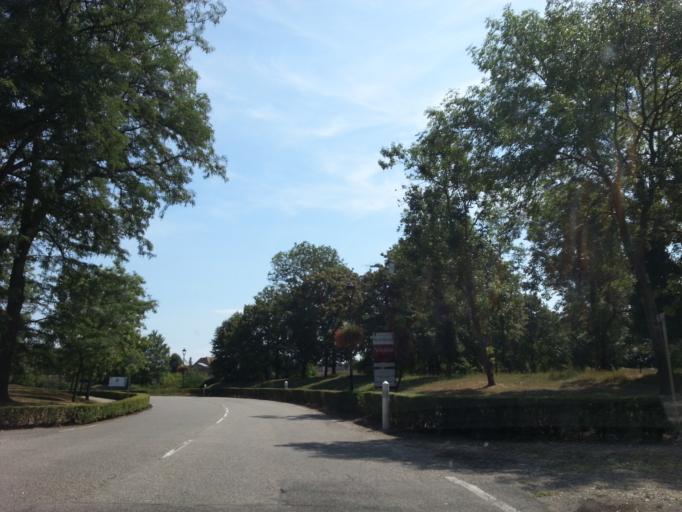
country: FR
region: Alsace
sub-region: Departement du Haut-Rhin
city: Neuf-Brisach
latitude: 48.0201
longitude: 7.5217
